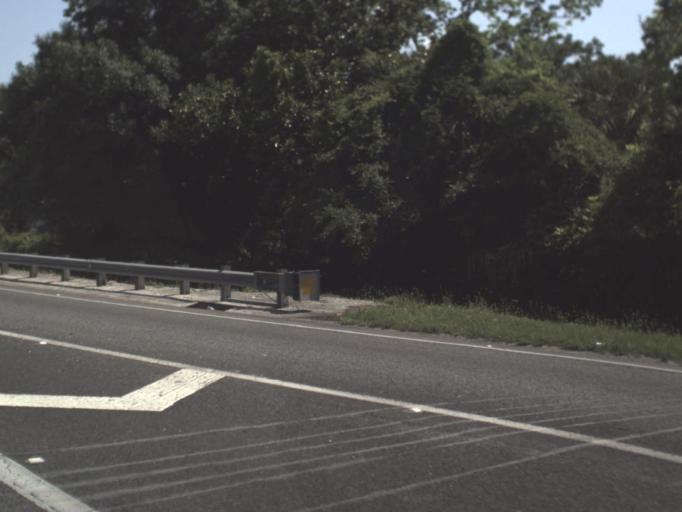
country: US
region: Florida
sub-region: Duval County
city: Jacksonville
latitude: 30.3492
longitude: -81.6683
